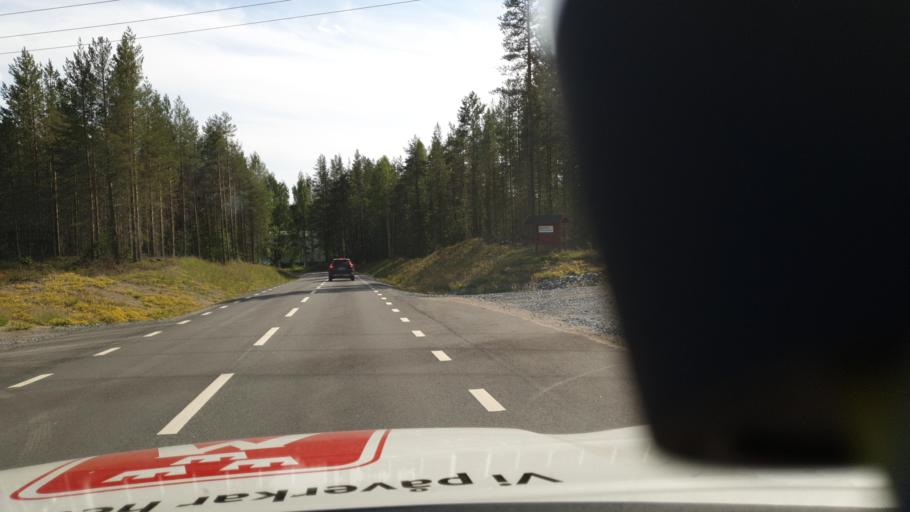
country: SE
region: Vaesterbotten
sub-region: Skelleftea Kommun
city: Boliden
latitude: 64.7972
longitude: 20.3350
